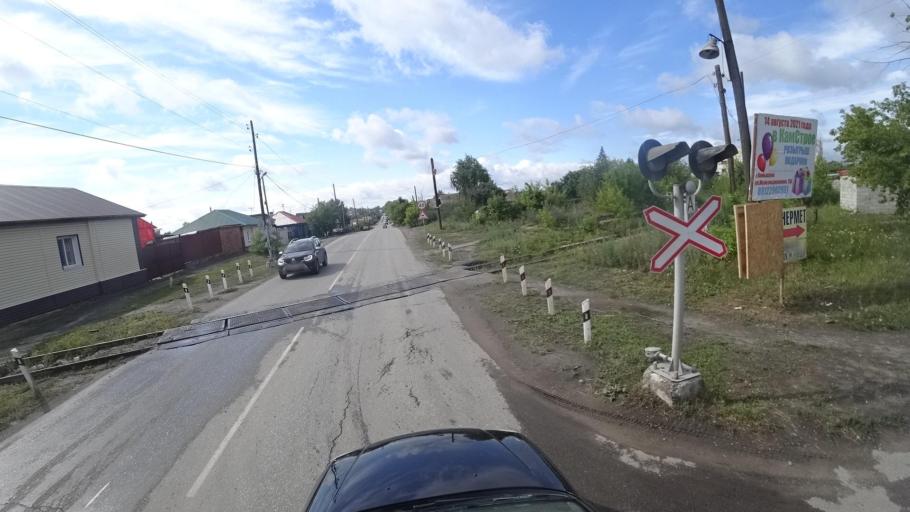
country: RU
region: Sverdlovsk
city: Kamyshlov
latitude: 56.8408
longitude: 62.7265
